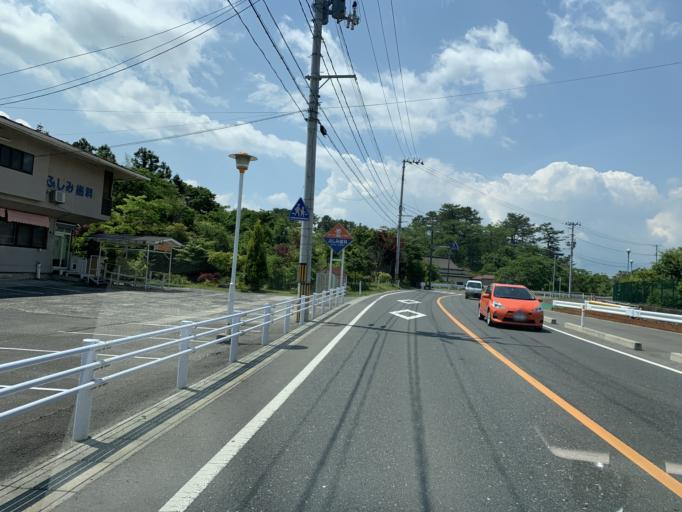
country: JP
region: Miyagi
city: Kogota
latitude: 38.5393
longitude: 141.0573
